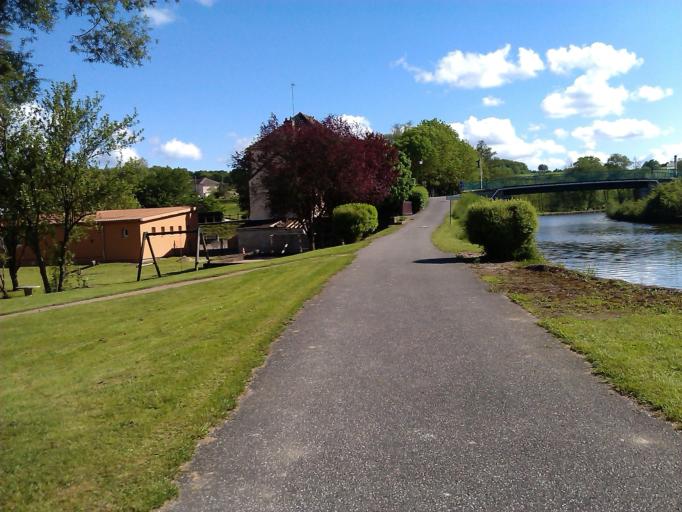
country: FR
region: Bourgogne
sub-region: Departement de Saone-et-Loire
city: Ecuisses
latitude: 46.7740
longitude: 4.5438
